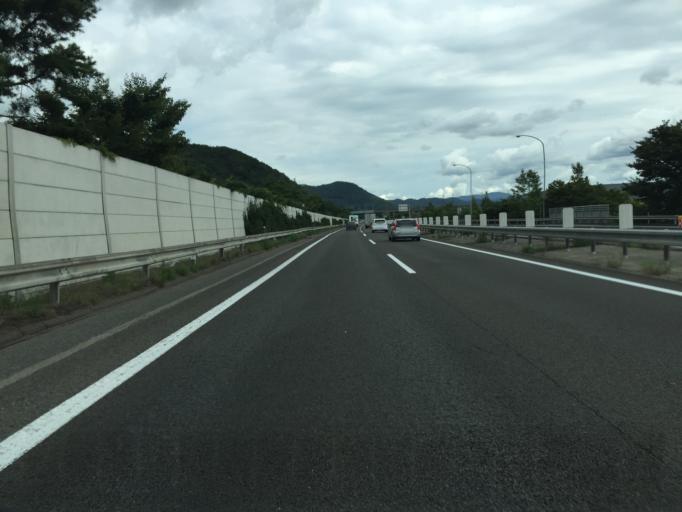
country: JP
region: Fukushima
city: Hobaramachi
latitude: 37.8809
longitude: 140.5324
